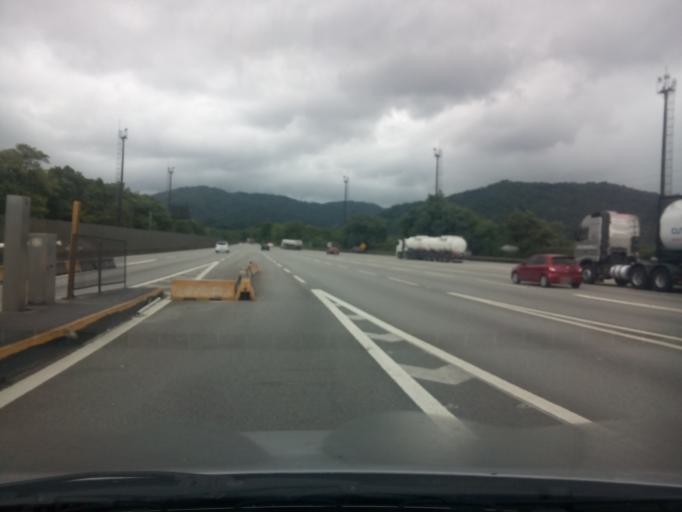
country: BR
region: Sao Paulo
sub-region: Santos
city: Santos
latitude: -23.8948
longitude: -46.3023
